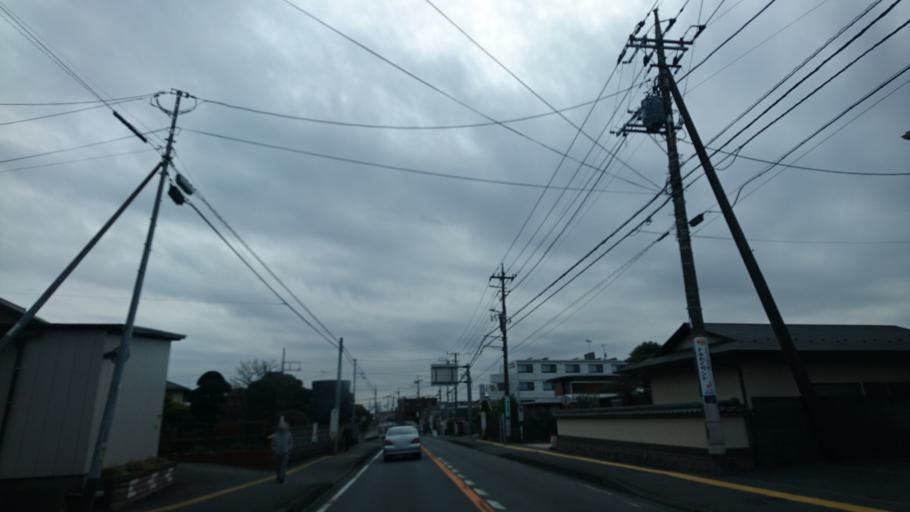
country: JP
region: Tokyo
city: Hachioji
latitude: 35.5800
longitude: 139.3327
